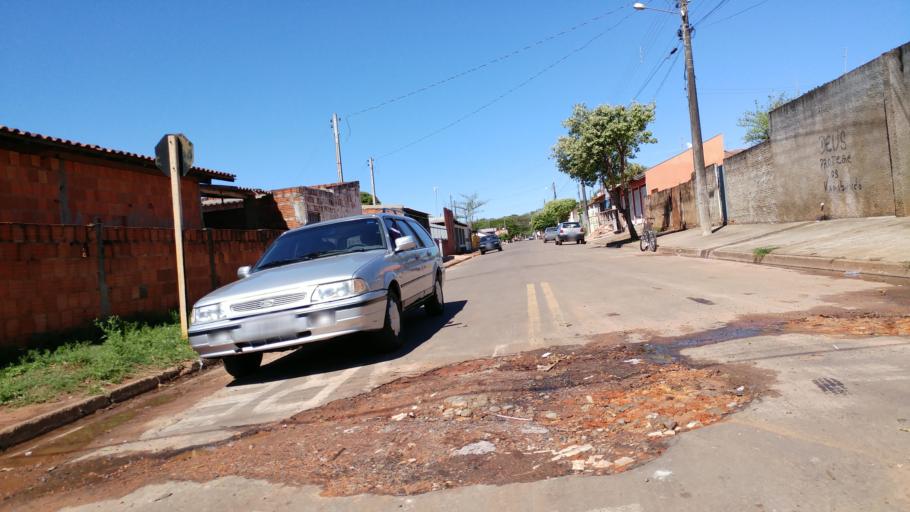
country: BR
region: Sao Paulo
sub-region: Paraguacu Paulista
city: Paraguacu Paulista
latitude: -22.4172
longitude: -50.5677
